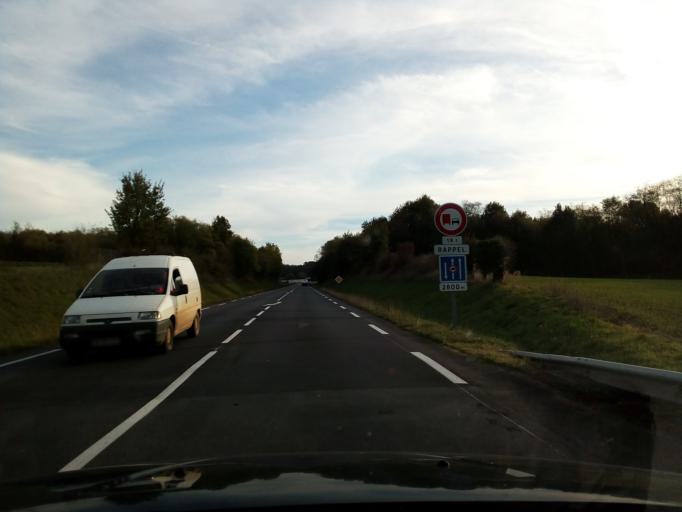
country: FR
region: Poitou-Charentes
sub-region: Departement de la Charente
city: Saint-Claud
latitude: 45.8656
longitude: 0.4659
